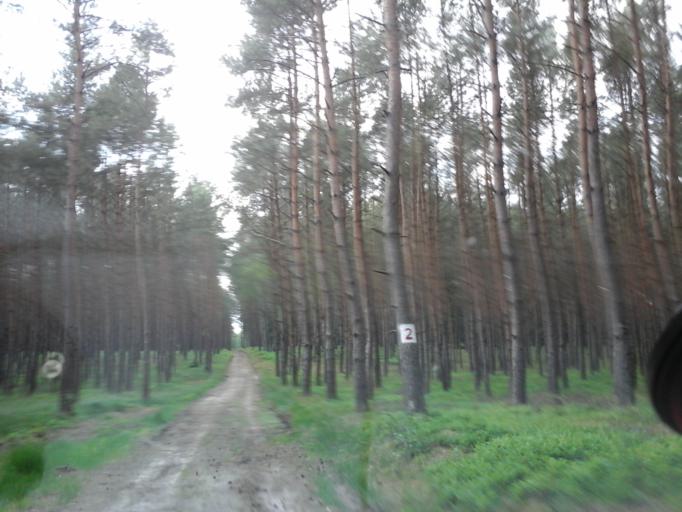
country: PL
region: West Pomeranian Voivodeship
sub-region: Powiat choszczenski
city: Drawno
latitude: 53.1130
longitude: 15.7830
